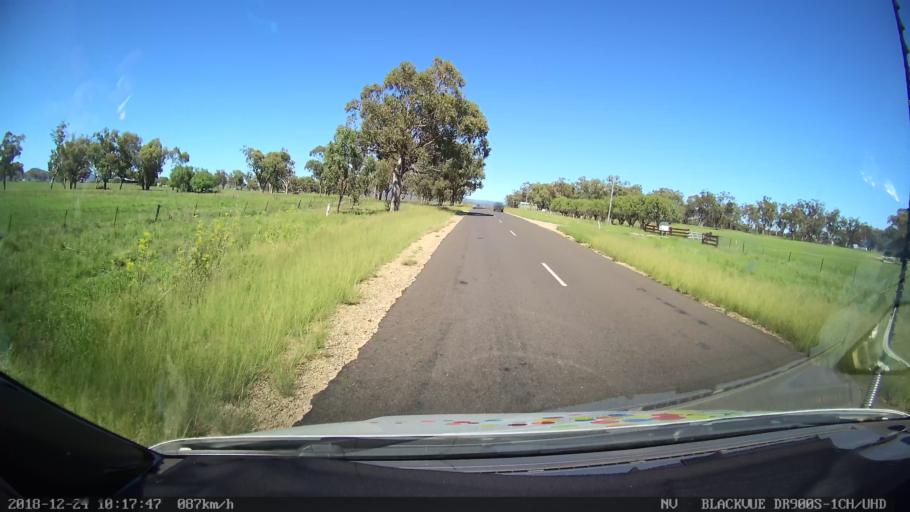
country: AU
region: New South Wales
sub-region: Liverpool Plains
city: Quirindi
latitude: -31.7213
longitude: 150.5862
